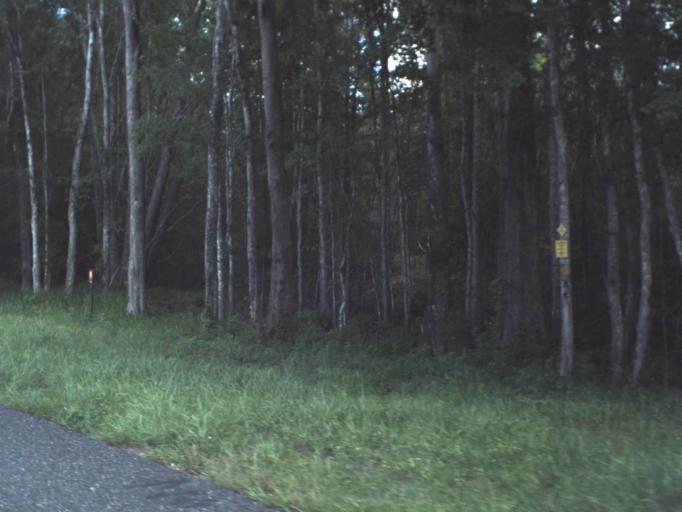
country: US
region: Florida
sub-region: Taylor County
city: Perry
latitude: 30.2563
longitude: -83.7055
